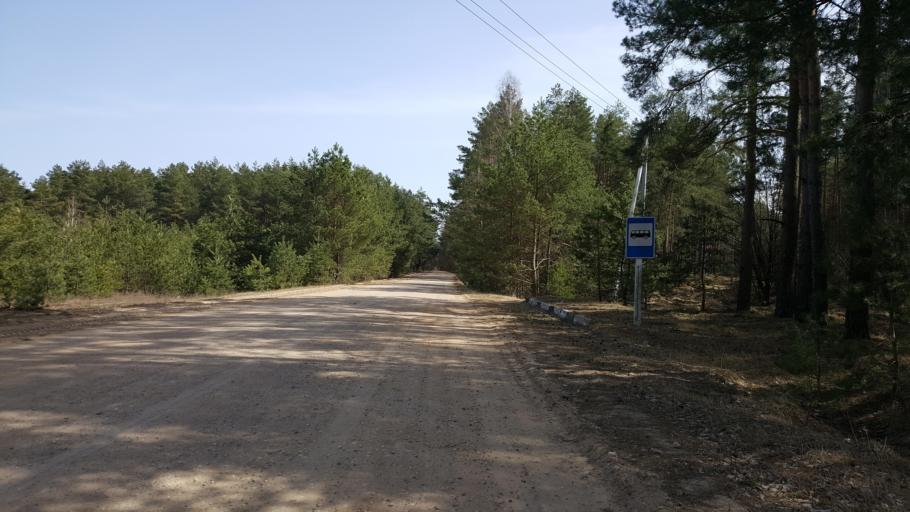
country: BY
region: Brest
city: Kamyanyuki
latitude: 52.5632
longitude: 23.7755
